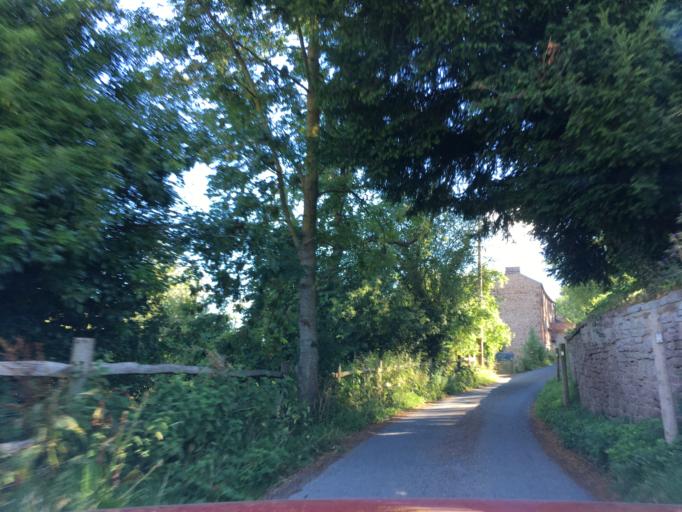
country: GB
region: England
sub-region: Herefordshire
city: Brockhampton
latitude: 51.9552
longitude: -2.5683
